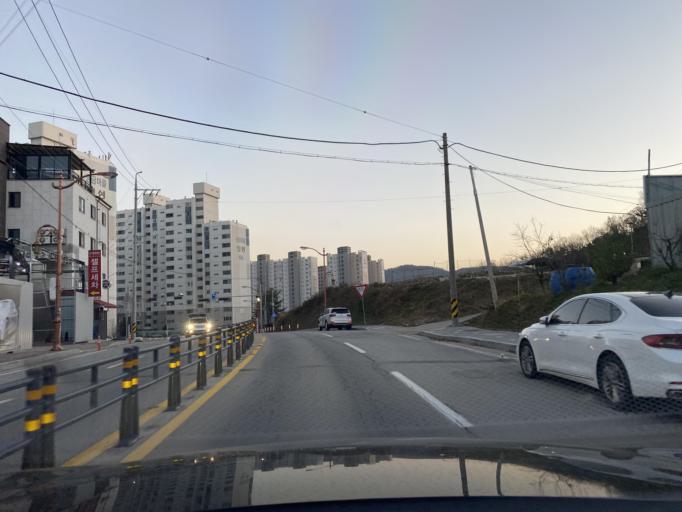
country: KR
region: Chungcheongnam-do
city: Yesan
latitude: 36.6856
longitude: 126.8432
